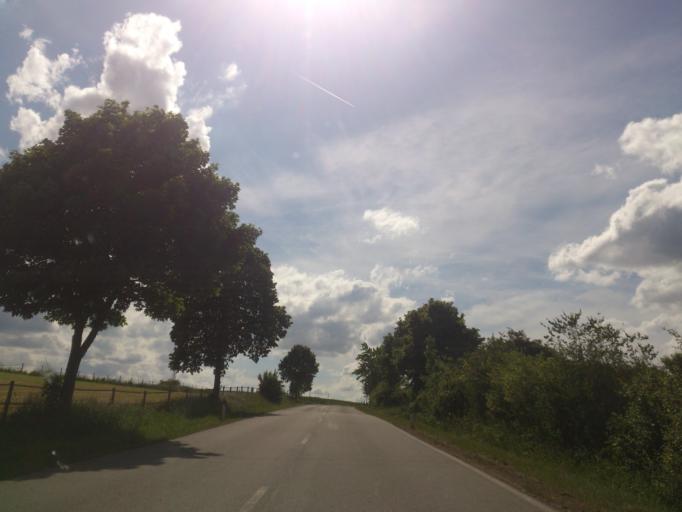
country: DE
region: North Rhine-Westphalia
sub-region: Regierungsbezirk Detmold
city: Willebadessen
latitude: 51.6553
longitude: 9.1054
